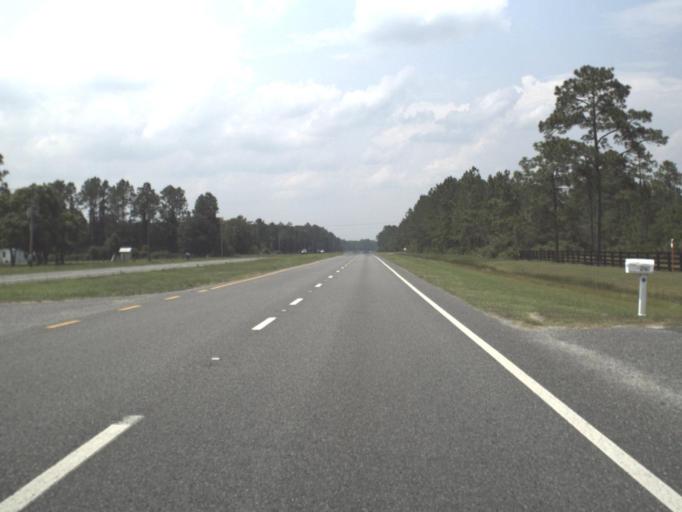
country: US
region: Florida
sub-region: Putnam County
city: East Palatka
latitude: 29.7918
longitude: -81.6492
